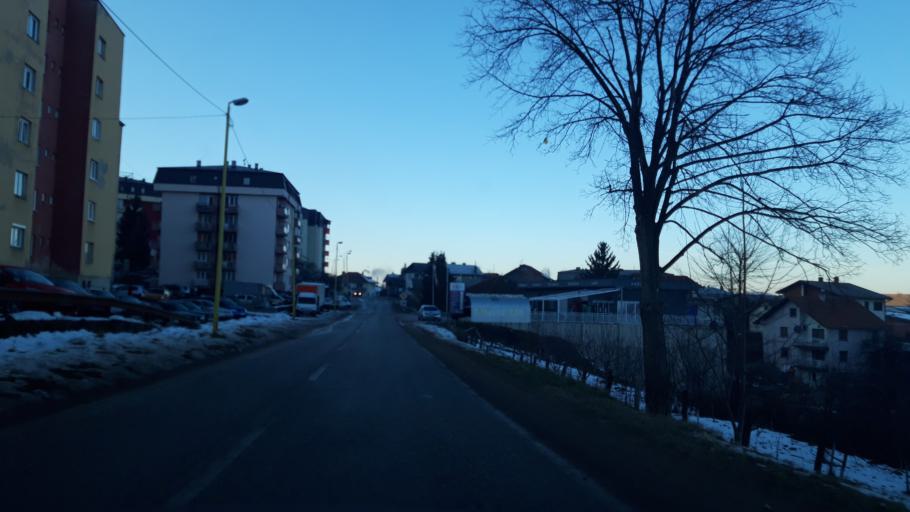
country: BA
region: Republika Srpska
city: Vlasenica
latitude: 44.1819
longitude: 18.9453
